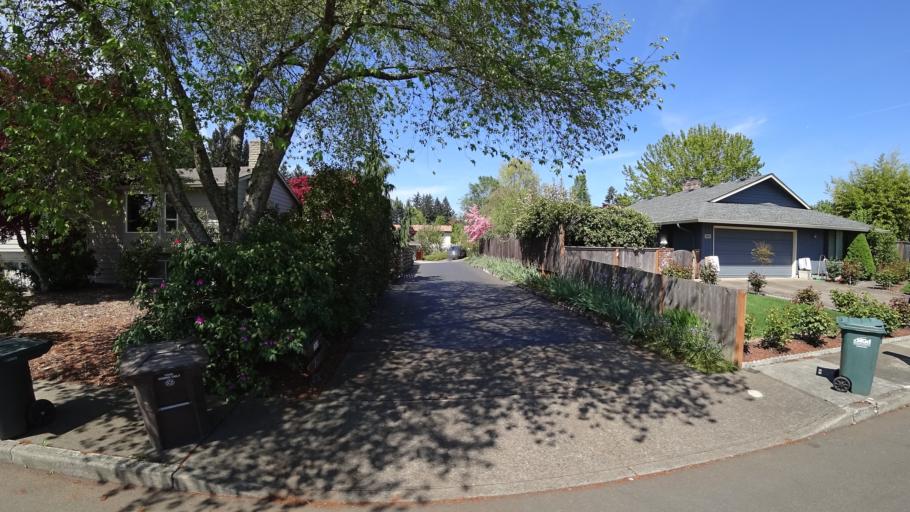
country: US
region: Oregon
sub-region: Washington County
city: Hillsboro
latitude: 45.5146
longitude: -122.9538
